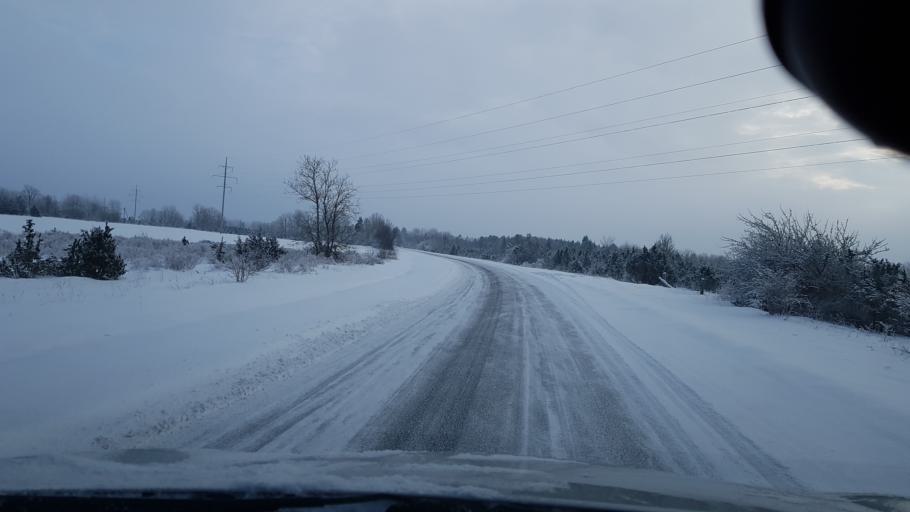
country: EE
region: Harju
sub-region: Keila linn
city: Keila
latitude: 59.3507
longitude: 24.4278
